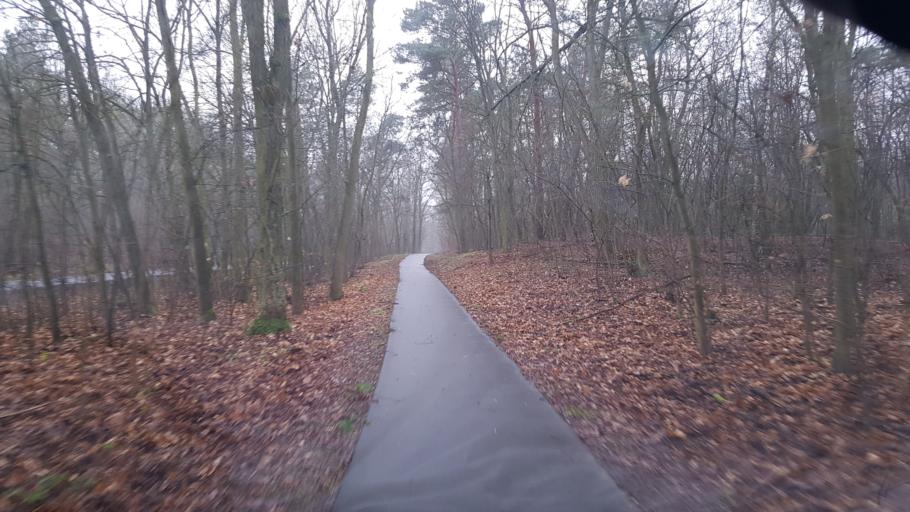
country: DE
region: Brandenburg
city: Stahnsdorf
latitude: 52.3557
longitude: 13.1830
